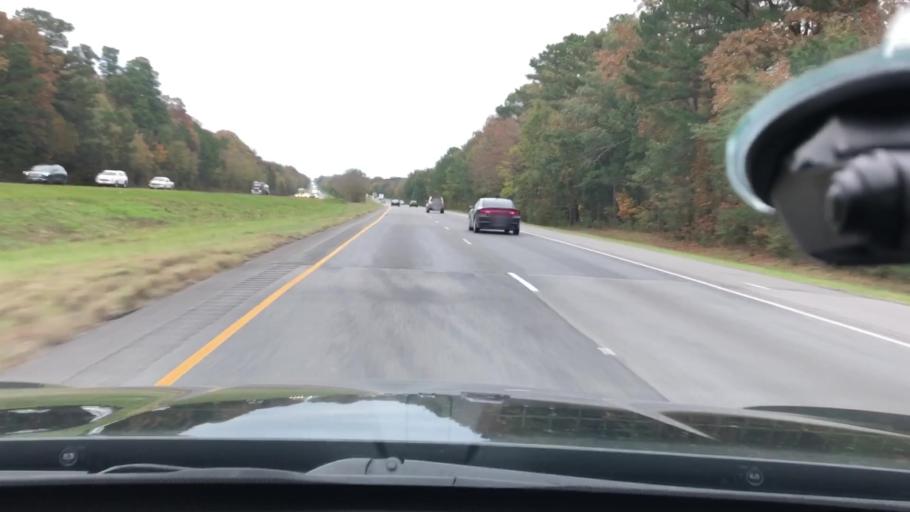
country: US
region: Arkansas
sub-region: Hempstead County
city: Hope
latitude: 33.6303
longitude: -93.7259
